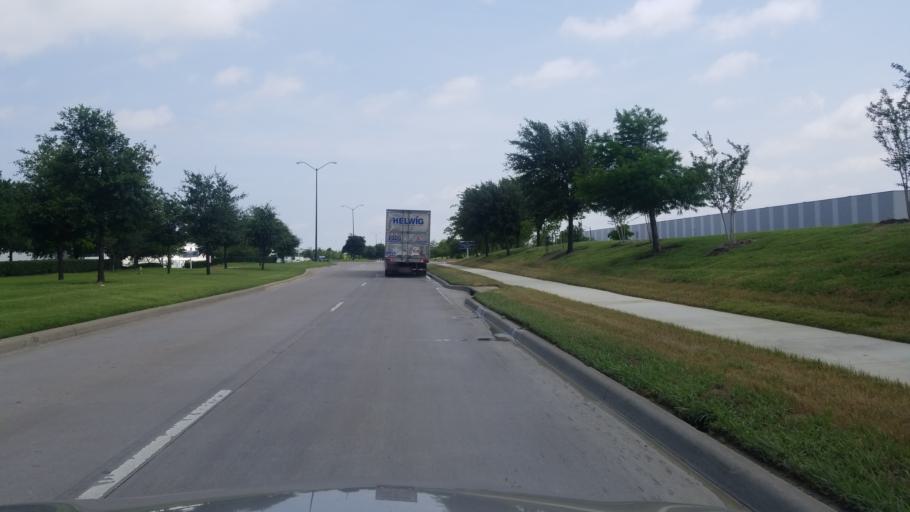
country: US
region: Texas
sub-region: Dallas County
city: Duncanville
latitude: 32.6821
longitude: -96.9649
